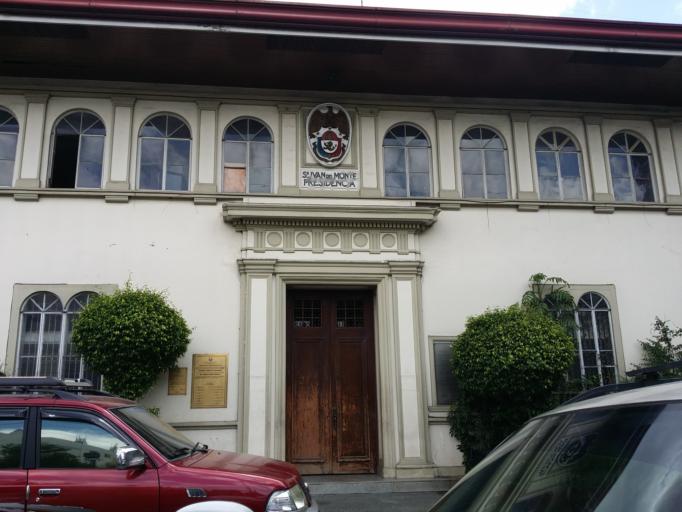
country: PH
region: Metro Manila
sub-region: San Juan
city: San Juan
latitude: 14.6064
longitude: 121.0239
